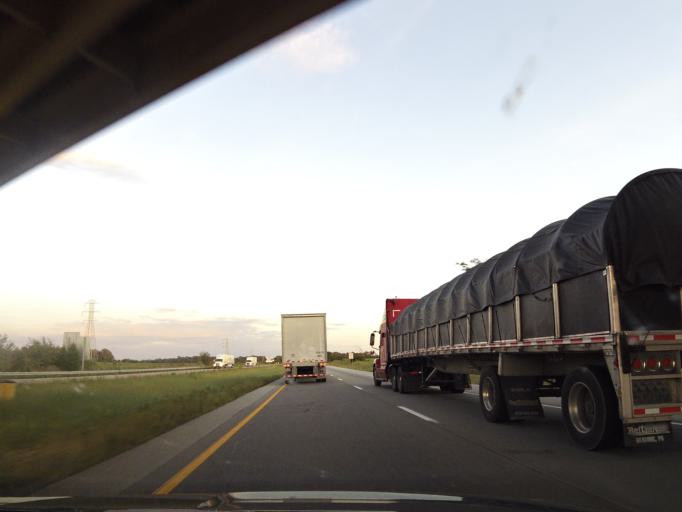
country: US
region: Indiana
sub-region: Shelby County
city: Shelbyville
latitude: 39.5189
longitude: -85.7226
